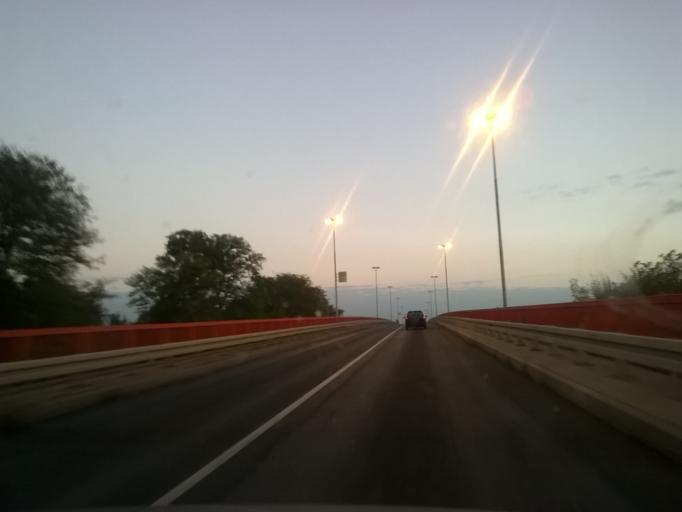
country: RS
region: Autonomna Pokrajina Vojvodina
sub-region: Juznobanatski Okrug
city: Pancevo
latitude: 44.8899
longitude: 20.6311
